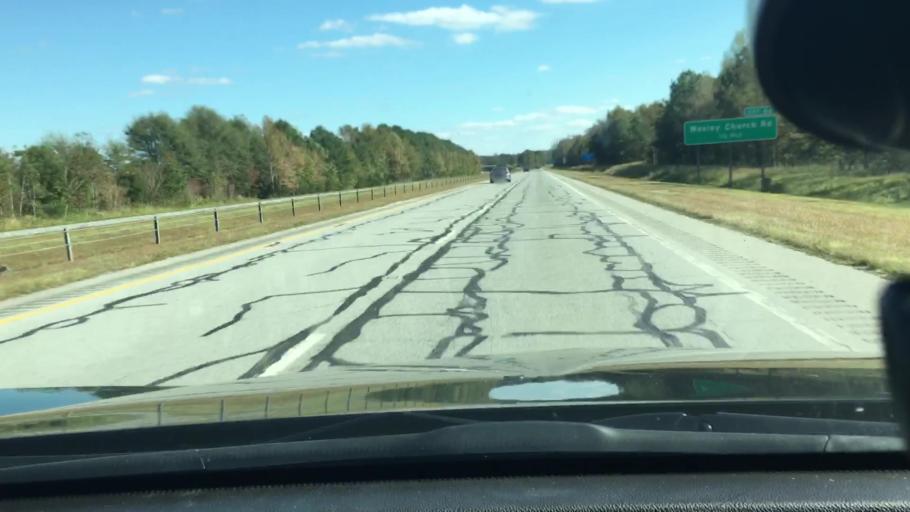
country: US
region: North Carolina
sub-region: Pitt County
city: Farmville
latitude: 35.6049
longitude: -77.5683
